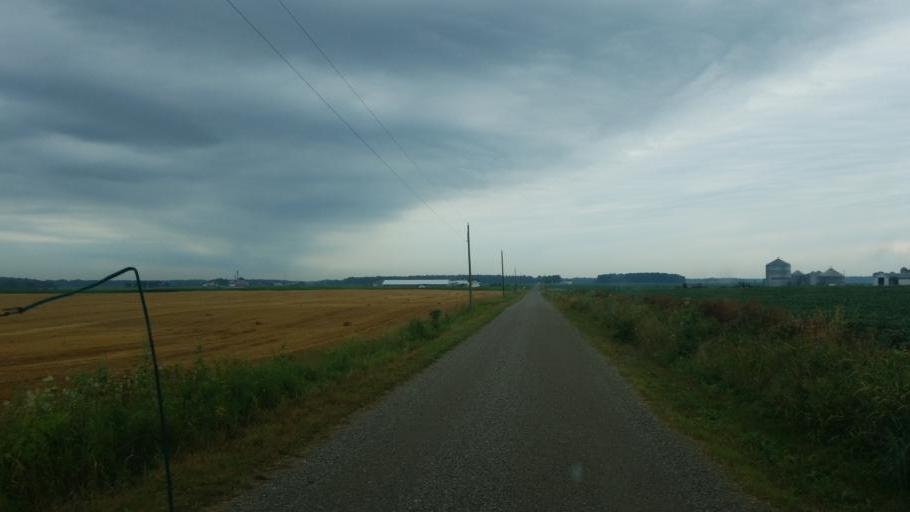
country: US
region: Indiana
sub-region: Steuben County
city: Hamilton
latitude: 41.4751
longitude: -84.9104
